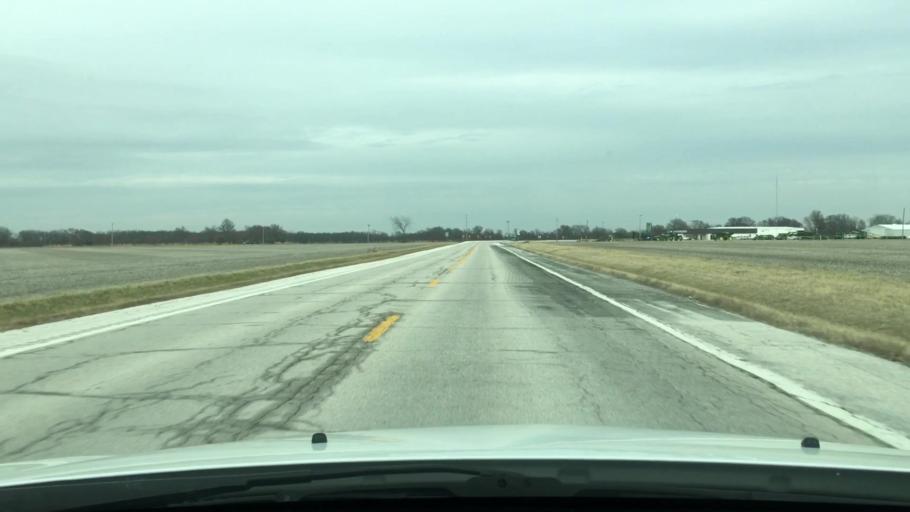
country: US
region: Missouri
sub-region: Audrain County
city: Vandalia
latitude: 39.3433
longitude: -91.4165
